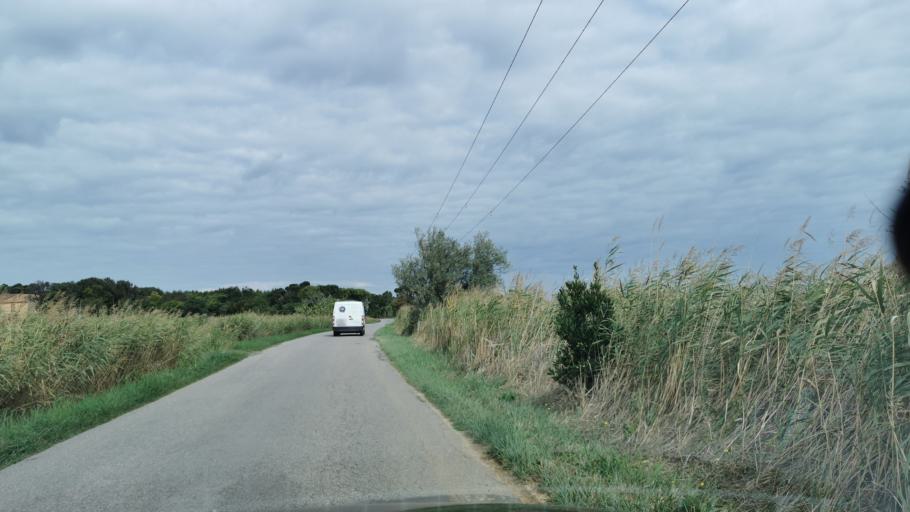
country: FR
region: Languedoc-Roussillon
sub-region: Departement de l'Aude
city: Fleury
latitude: 43.2011
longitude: 3.1911
